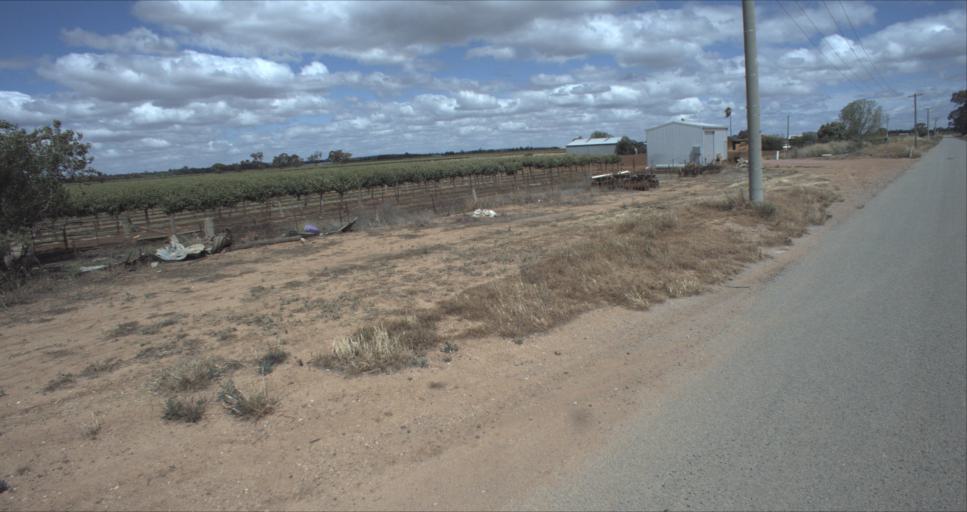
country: AU
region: New South Wales
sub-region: Leeton
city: Leeton
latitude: -34.5719
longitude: 146.3990
